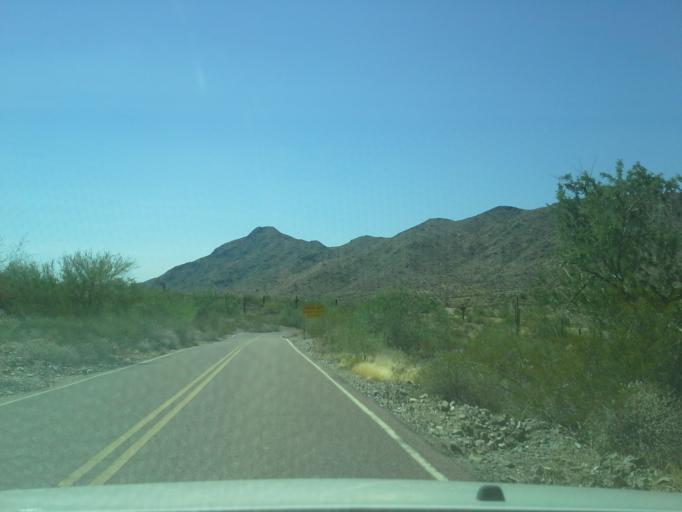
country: US
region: Arizona
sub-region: Maricopa County
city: Laveen
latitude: 33.3326
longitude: -112.0957
